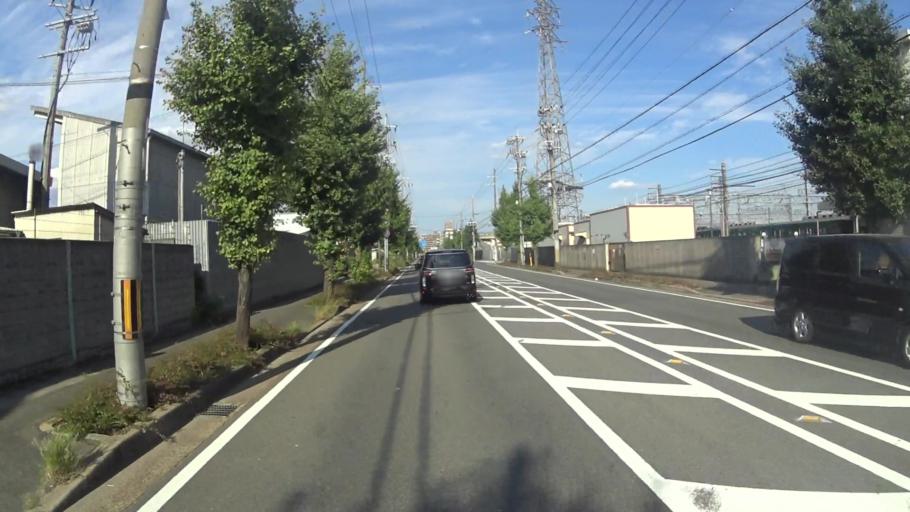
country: JP
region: Kyoto
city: Yawata
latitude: 34.8995
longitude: 135.7080
